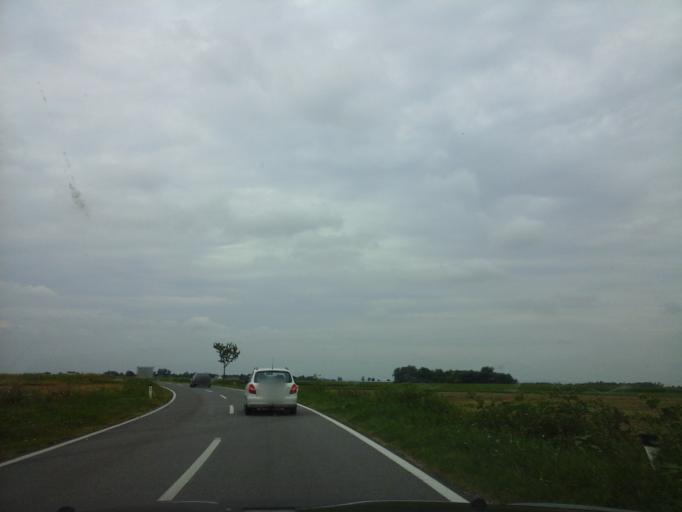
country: AT
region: Lower Austria
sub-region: Politischer Bezirk Ganserndorf
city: Haringsee
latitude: 48.1656
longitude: 16.7762
